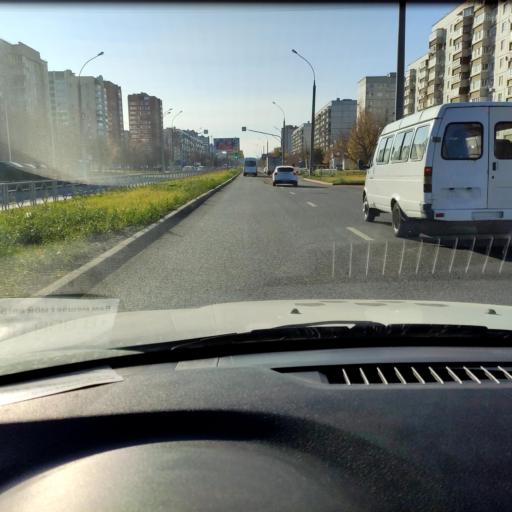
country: RU
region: Samara
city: Tol'yatti
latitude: 53.5482
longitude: 49.3321
